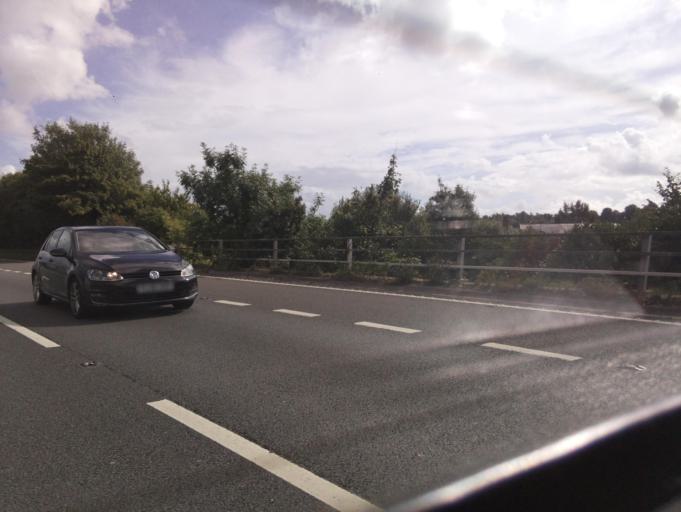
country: GB
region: England
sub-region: Borough of Stockport
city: Stockport
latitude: 53.4147
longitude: -2.1551
